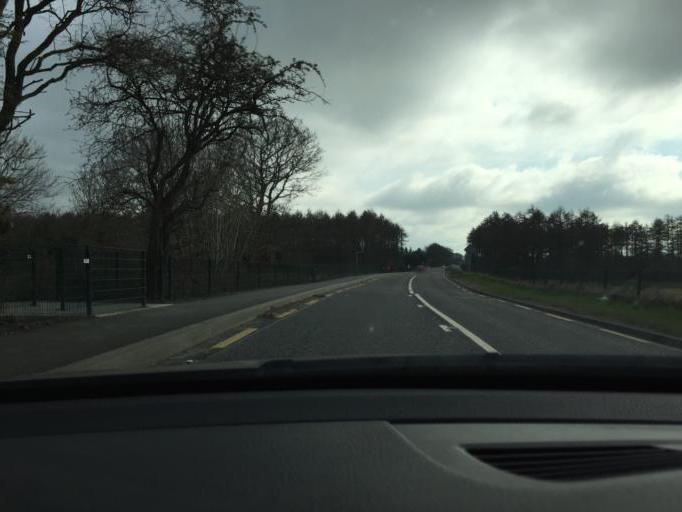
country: IE
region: Leinster
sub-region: Wicklow
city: Blessington
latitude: 53.1577
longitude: -6.5518
